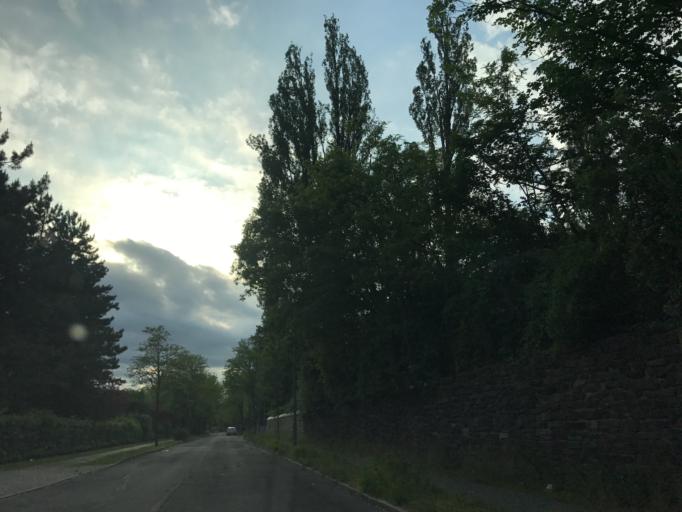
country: DE
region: Berlin
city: Westend
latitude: 52.5060
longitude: 13.2685
